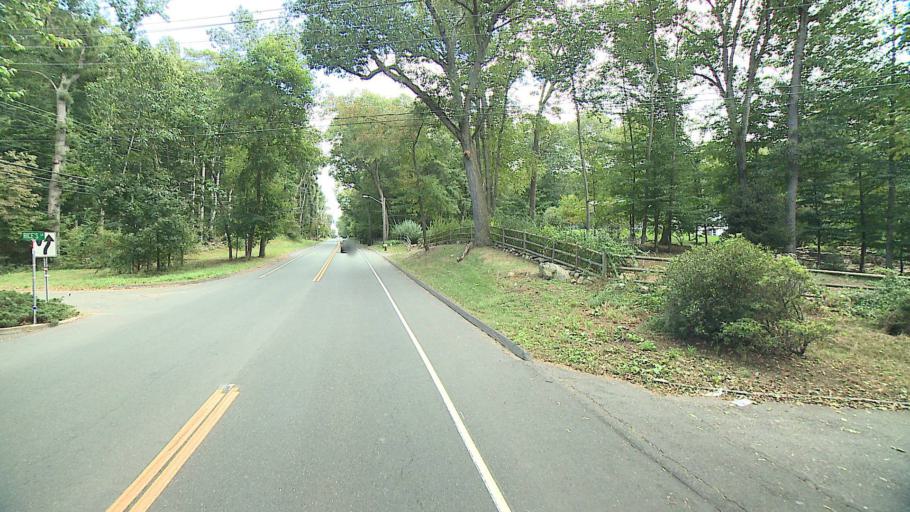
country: US
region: Connecticut
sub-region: Fairfield County
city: Westport
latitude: 41.1584
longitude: -73.3744
